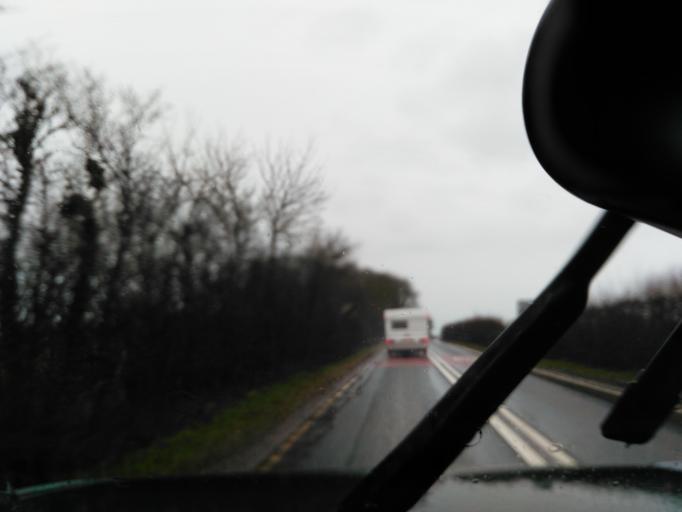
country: GB
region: England
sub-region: Somerset
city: Evercreech
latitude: 51.1876
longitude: -2.4856
